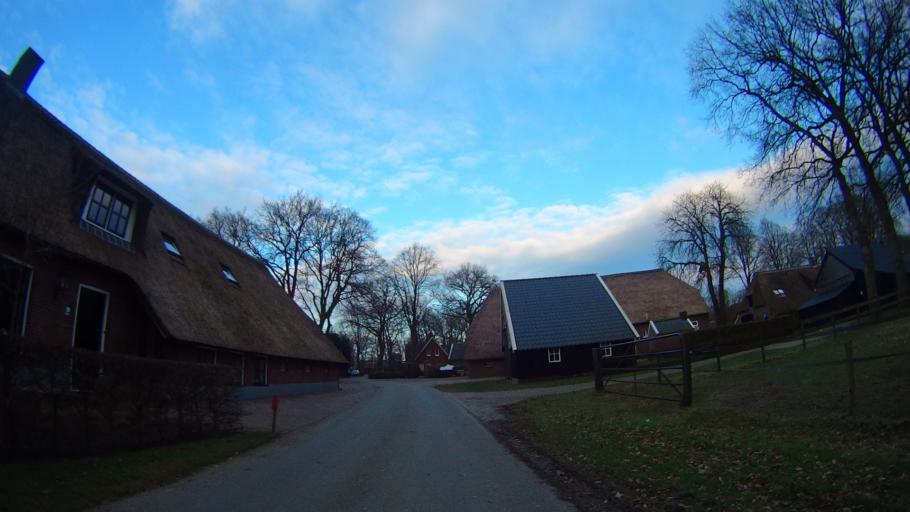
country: NL
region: Drenthe
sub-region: Gemeente Coevorden
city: Sleen
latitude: 52.7772
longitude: 6.7984
